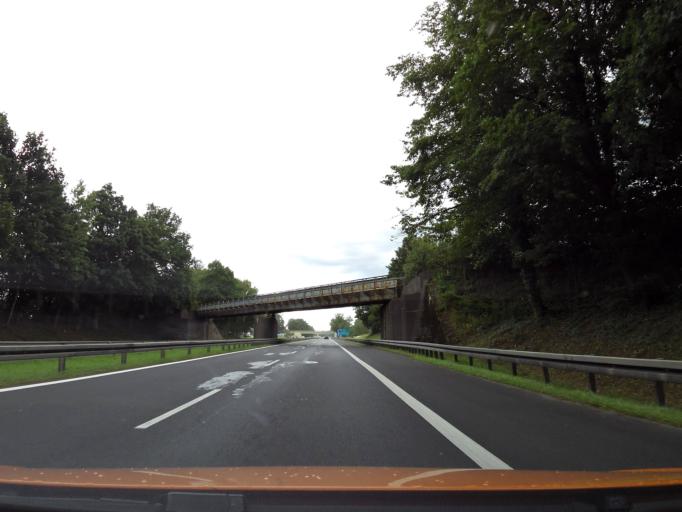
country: PL
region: West Pomeranian Voivodeship
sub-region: Powiat policki
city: Kolbaskowo
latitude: 53.3391
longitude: 14.4333
